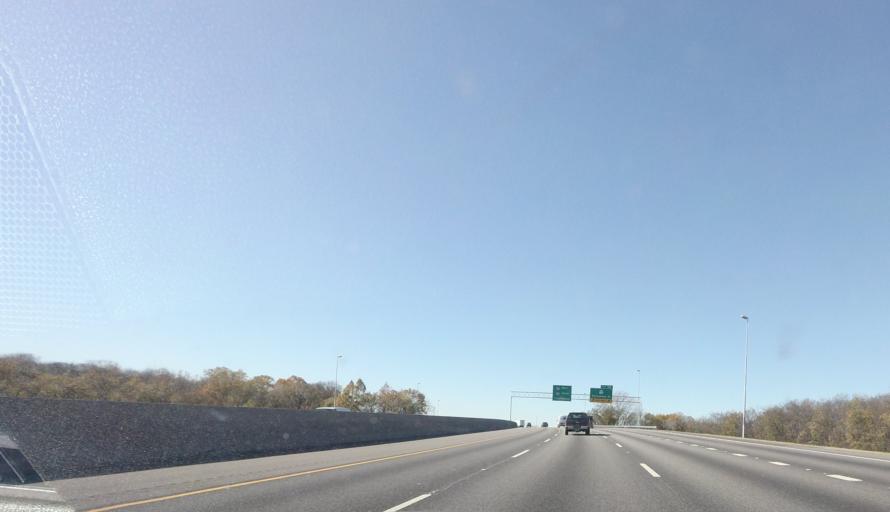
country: US
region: Alabama
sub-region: Jefferson County
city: Tarrant
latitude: 33.5503
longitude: -86.7722
